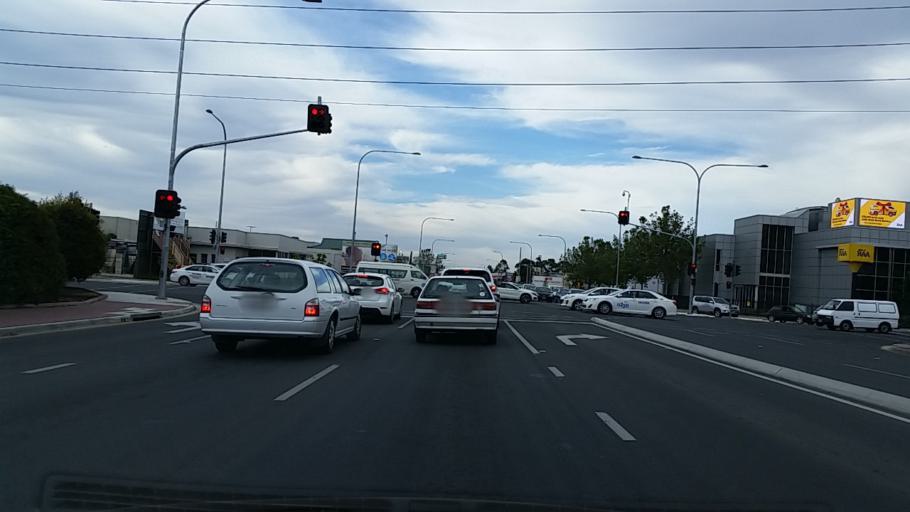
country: AU
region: South Australia
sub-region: Unley
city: Forestville
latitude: -34.9425
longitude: 138.5711
